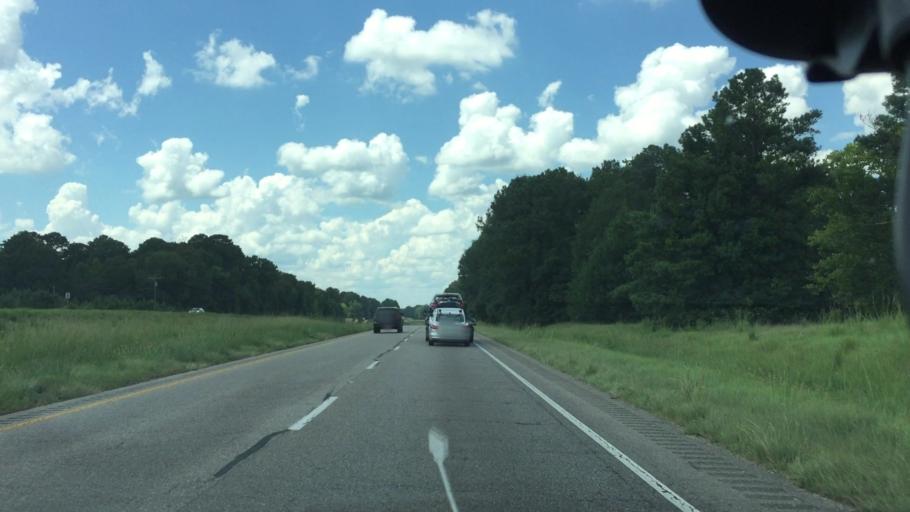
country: US
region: Alabama
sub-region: Montgomery County
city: Pike Road
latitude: 32.1282
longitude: -86.0807
